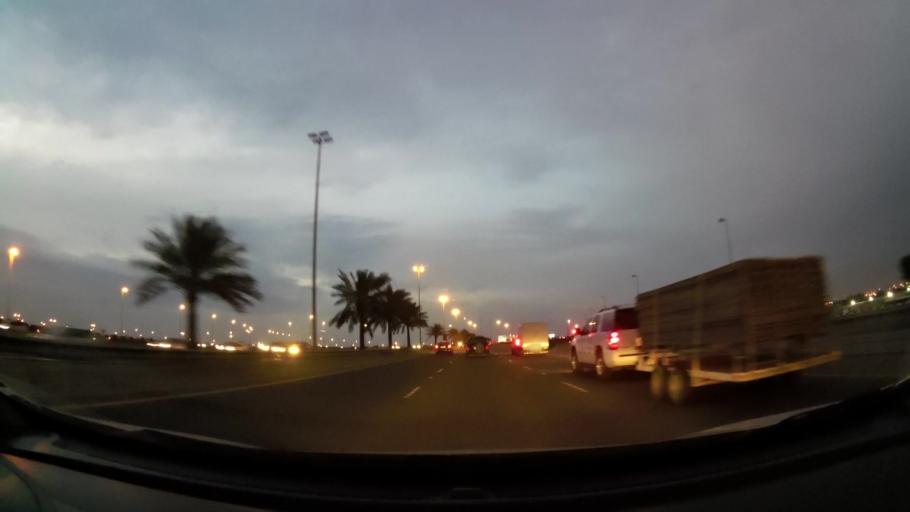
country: BH
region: Northern
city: Madinat `Isa
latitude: 26.1793
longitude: 50.5025
